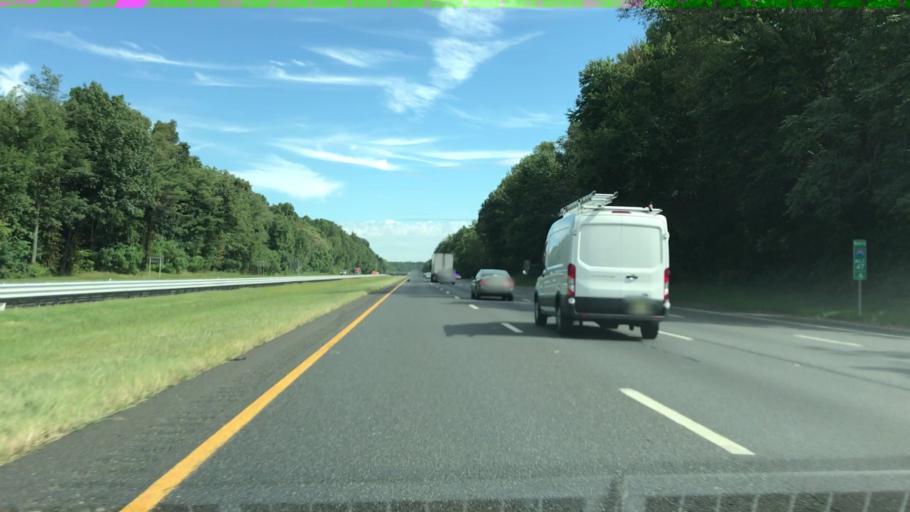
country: US
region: New Jersey
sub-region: Burlington County
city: Burlington
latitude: 40.0475
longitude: -74.8309
